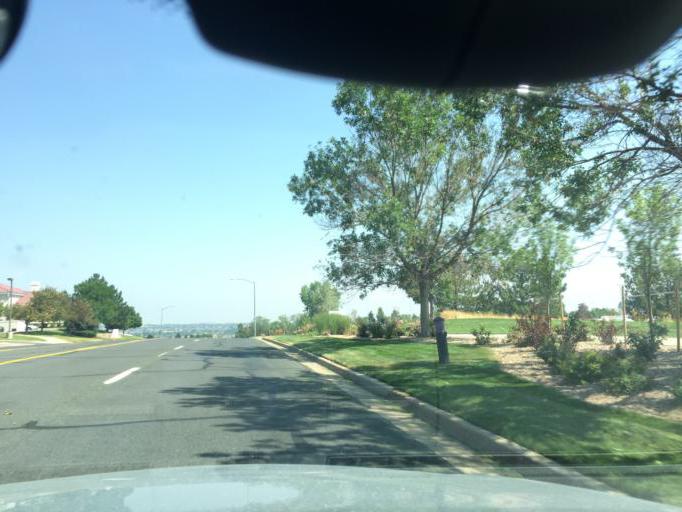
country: US
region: Colorado
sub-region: Adams County
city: Northglenn
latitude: 39.9099
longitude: -105.0060
